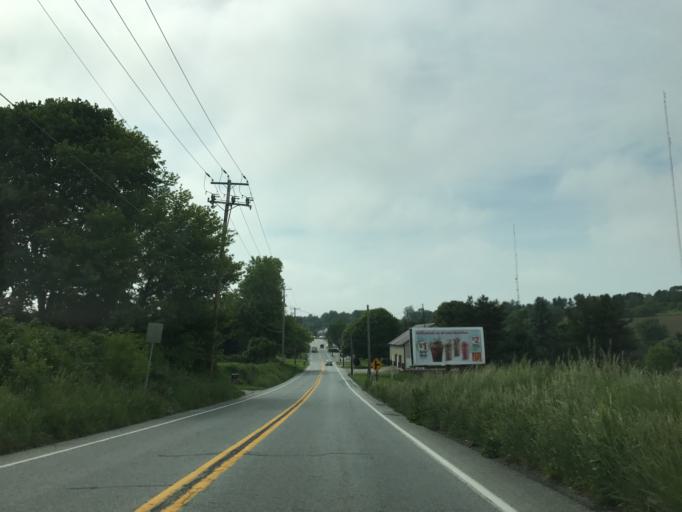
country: US
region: Pennsylvania
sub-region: York County
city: Windsor
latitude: 39.9004
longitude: -76.5760
